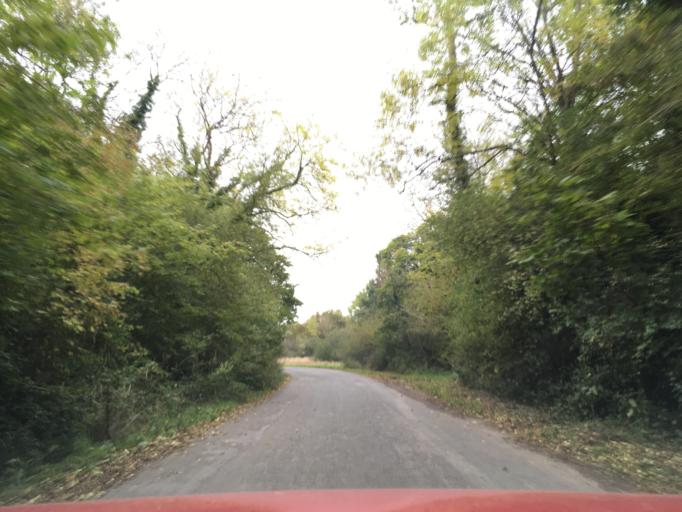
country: GB
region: England
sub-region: South Gloucestershire
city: Horton
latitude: 51.5924
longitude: -2.3582
